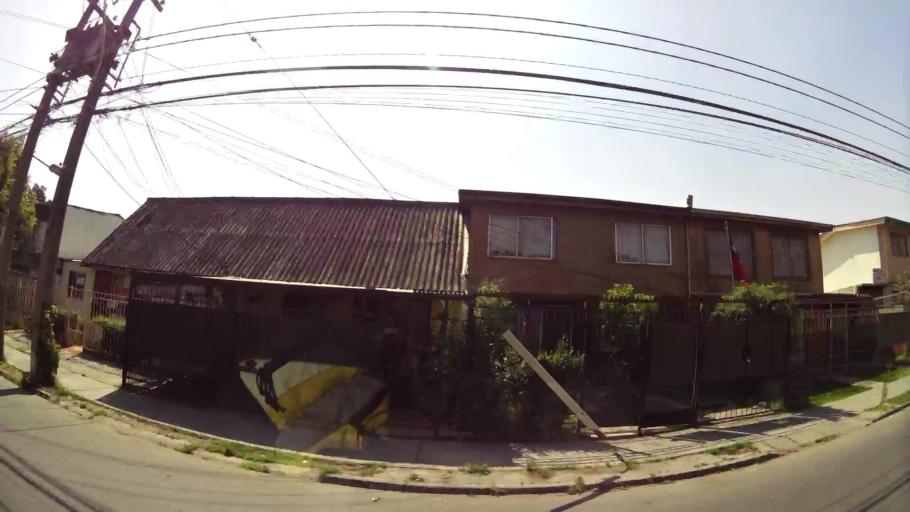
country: CL
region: Santiago Metropolitan
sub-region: Provincia de Santiago
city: La Pintana
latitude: -33.5506
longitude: -70.6086
